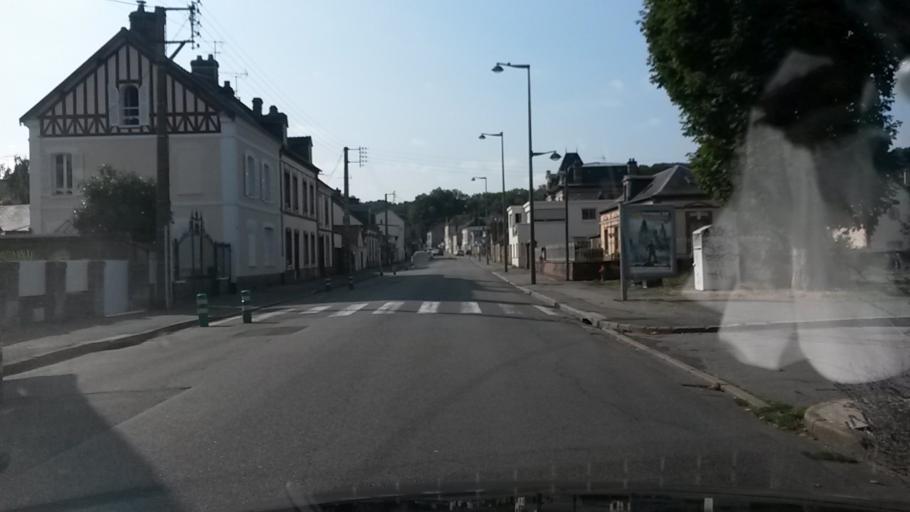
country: FR
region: Haute-Normandie
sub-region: Departement de l'Eure
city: Evreux
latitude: 49.0209
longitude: 1.1415
